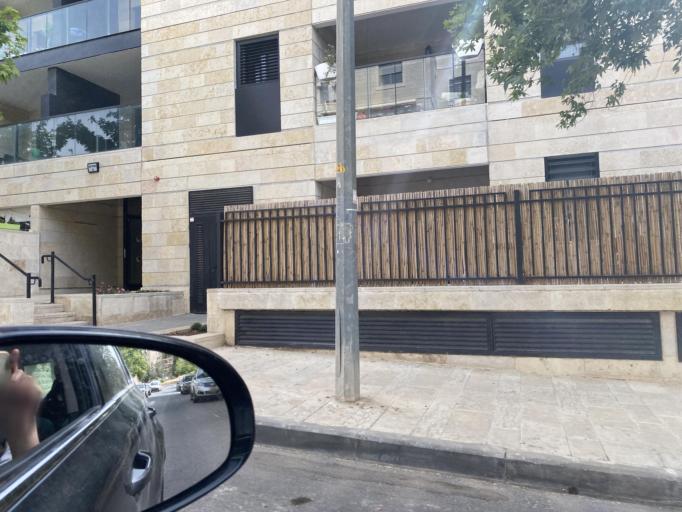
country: IL
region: Jerusalem
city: Jerusalem
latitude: 31.7566
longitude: 35.2264
